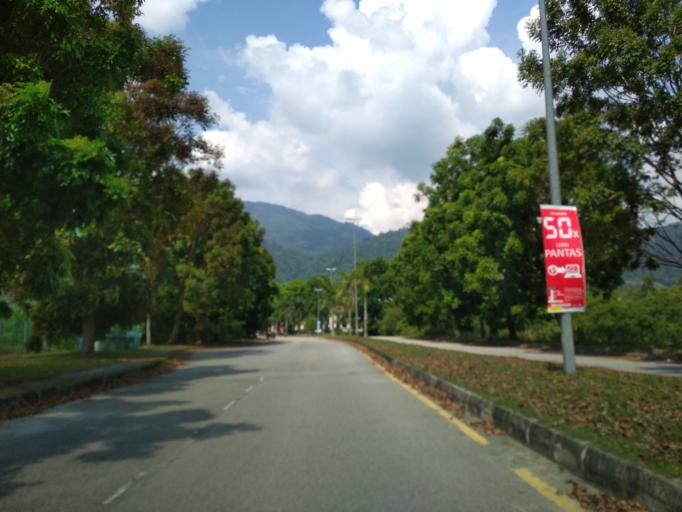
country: MY
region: Perak
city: Kampar
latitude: 4.3358
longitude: 101.1488
